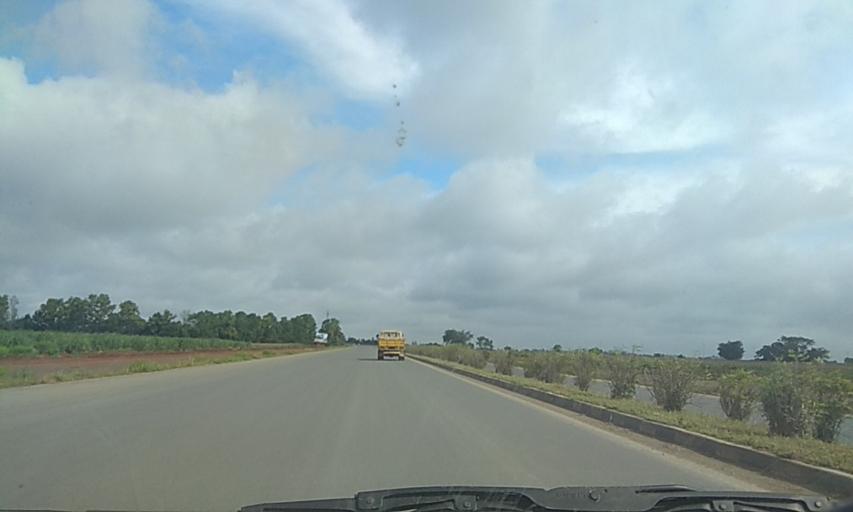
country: IN
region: Karnataka
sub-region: Haveri
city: Shiggaon
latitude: 15.0499
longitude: 75.1687
